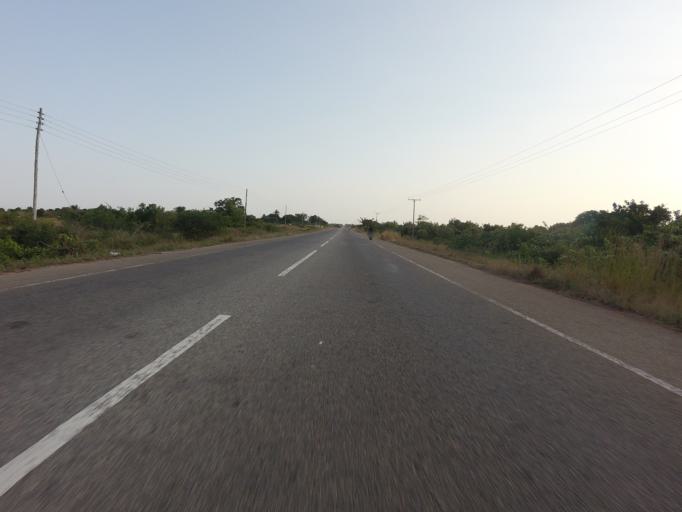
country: GH
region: Volta
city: Anloga
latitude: 6.0321
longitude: 0.6039
